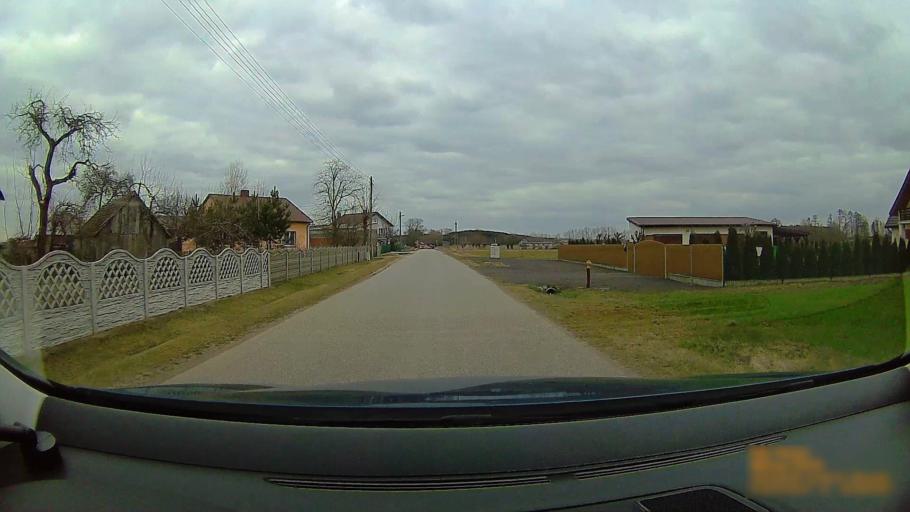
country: PL
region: Greater Poland Voivodeship
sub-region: Powiat koninski
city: Rzgow Pierwszy
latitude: 52.1294
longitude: 18.0686
